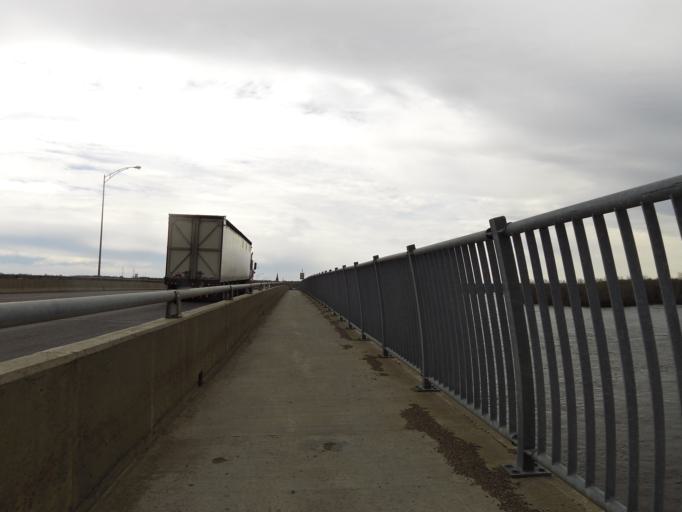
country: CA
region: Ontario
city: Hawkesbury
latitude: 45.6195
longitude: -74.5972
